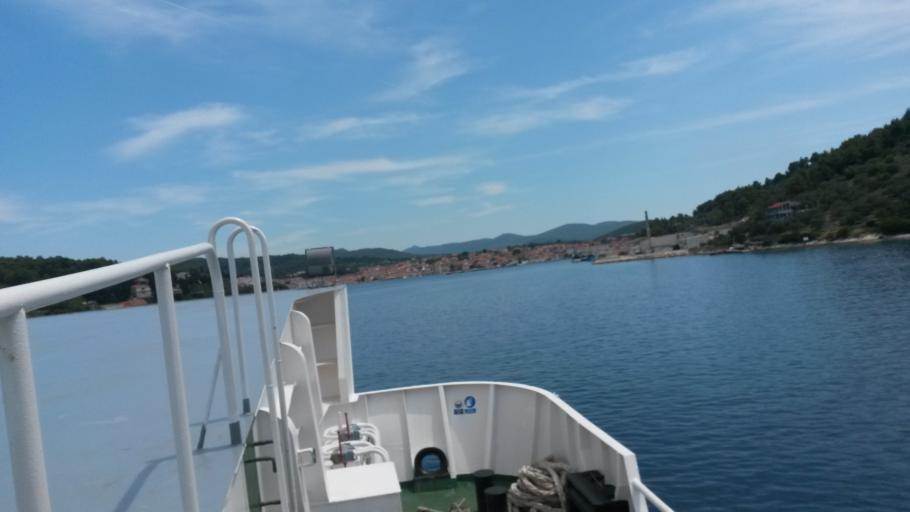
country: HR
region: Dubrovacko-Neretvanska
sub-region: Grad Dubrovnik
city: Vela Luka
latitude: 42.9618
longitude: 16.6986
